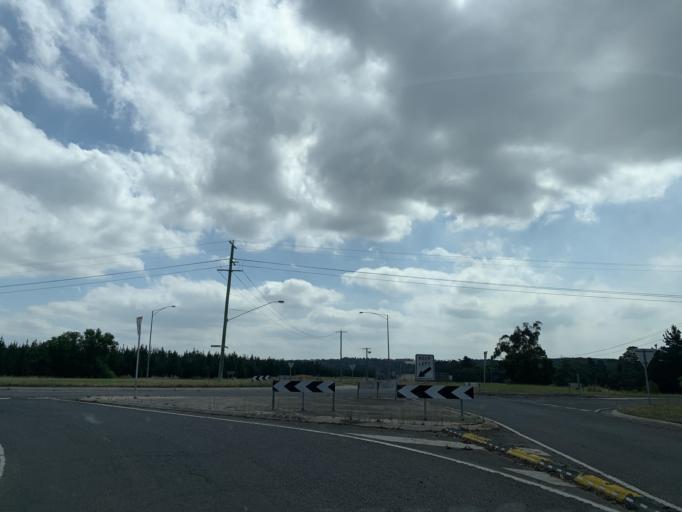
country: AU
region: Victoria
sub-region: Latrobe
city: Morwell
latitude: -38.2029
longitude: 146.4474
